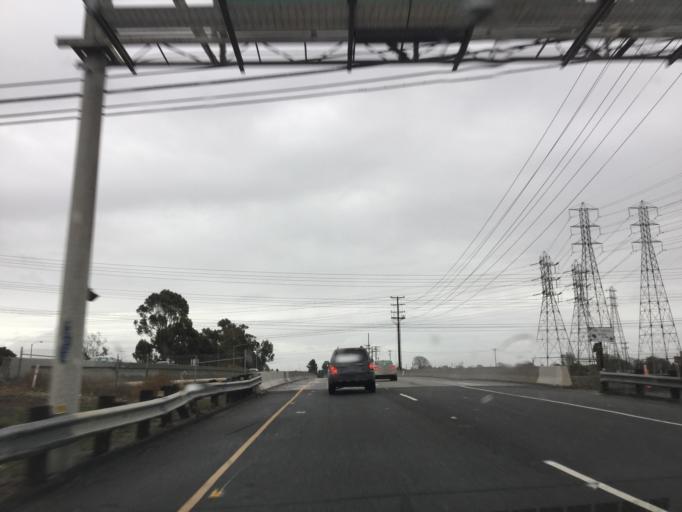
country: US
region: California
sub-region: Orange County
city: Rossmoor
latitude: 33.7743
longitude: -118.0988
